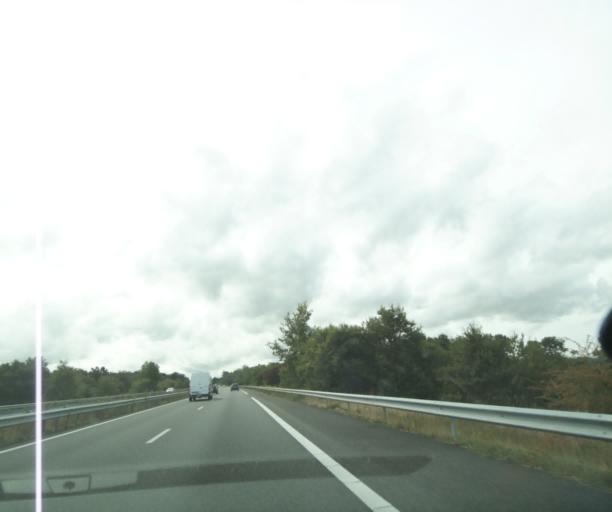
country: FR
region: Poitou-Charentes
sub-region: Departement de la Charente-Maritime
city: Saint-Genis-de-Saintonge
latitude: 45.4727
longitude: -0.6207
